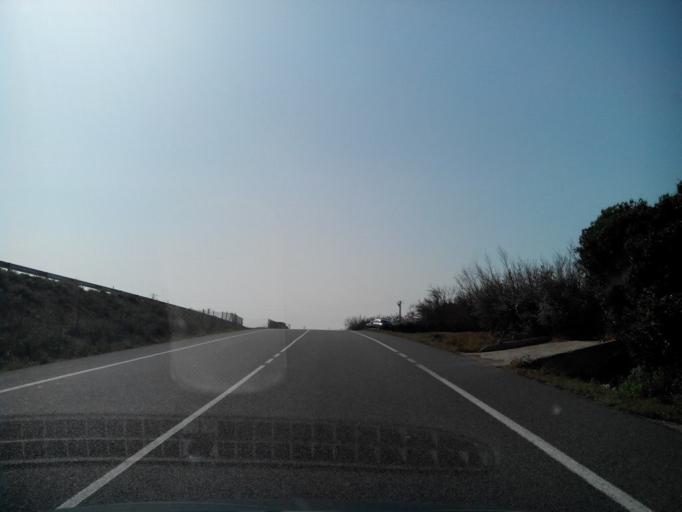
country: ES
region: Catalonia
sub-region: Provincia de Tarragona
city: Alcover
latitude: 41.2605
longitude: 1.1761
